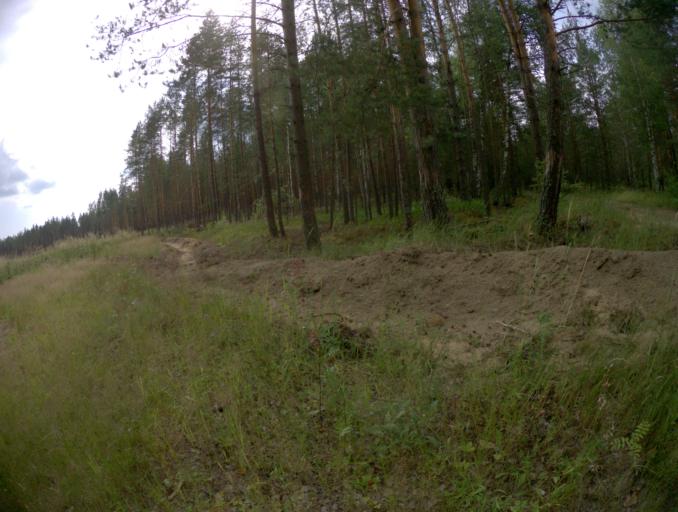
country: RU
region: Nizjnij Novgorod
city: Frolishchi
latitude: 56.3199
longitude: 42.6435
